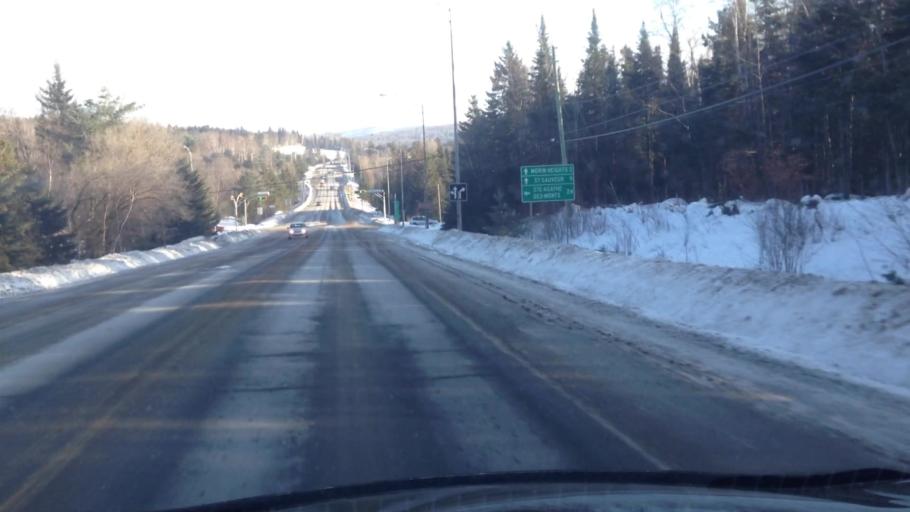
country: CA
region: Quebec
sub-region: Laurentides
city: Saint-Sauveur
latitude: 45.9092
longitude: -74.2621
